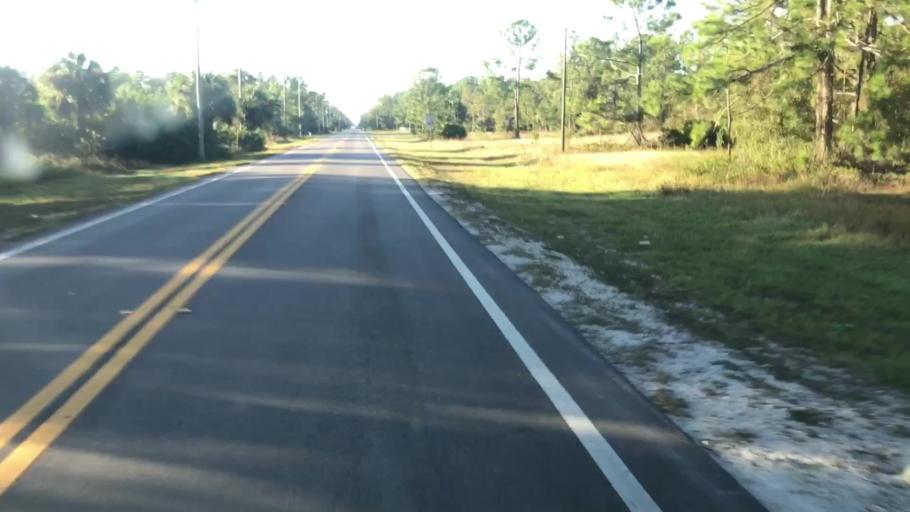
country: US
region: Florida
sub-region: Collier County
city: Orangetree
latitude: 26.2753
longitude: -81.6073
